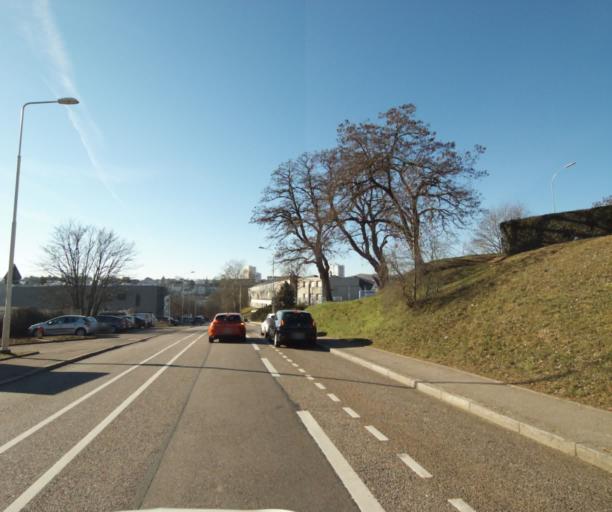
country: FR
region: Lorraine
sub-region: Departement de Meurthe-et-Moselle
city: Laxou
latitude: 48.6987
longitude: 6.1430
